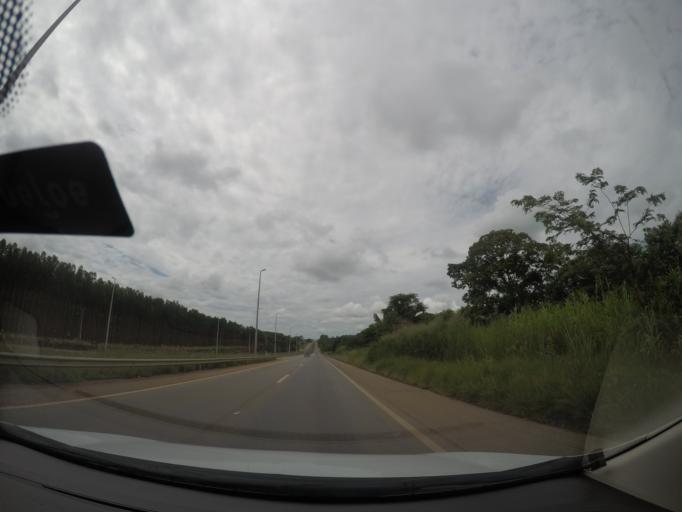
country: BR
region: Goias
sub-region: Goianira
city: Goianira
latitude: -16.4364
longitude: -49.4592
